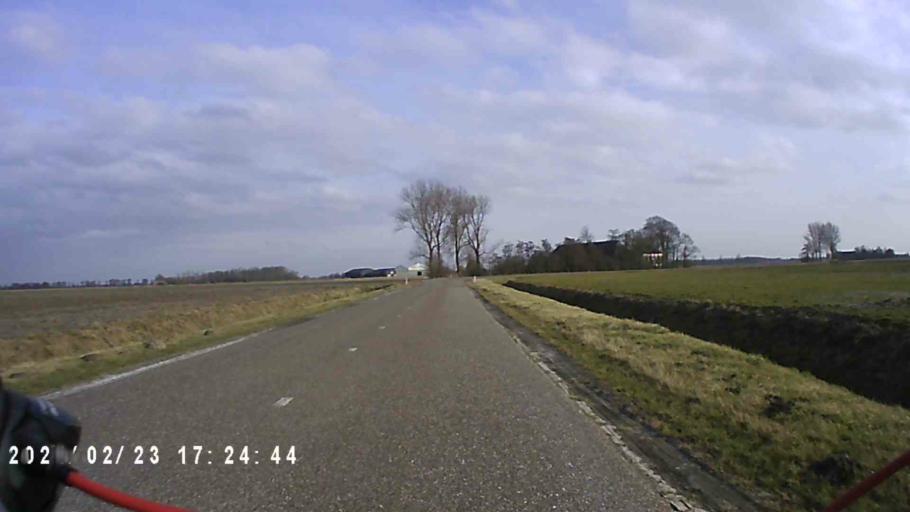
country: NL
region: Groningen
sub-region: Gemeente Winsum
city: Winsum
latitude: 53.3890
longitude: 6.4431
